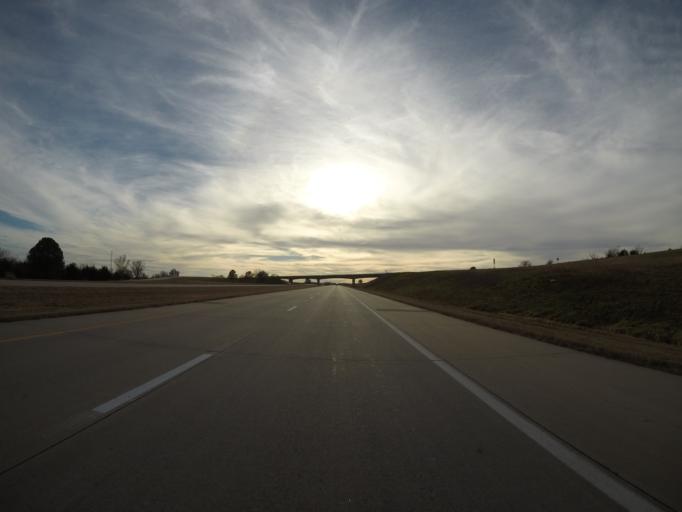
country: US
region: Kansas
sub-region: Franklin County
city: Ottawa
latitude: 38.5371
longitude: -95.3770
